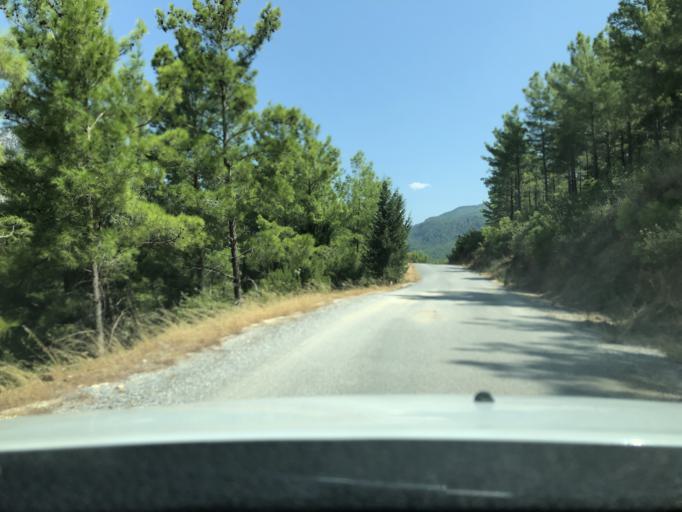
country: TR
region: Antalya
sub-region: Manavgat
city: Manavgat
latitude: 36.9119
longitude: 31.5468
